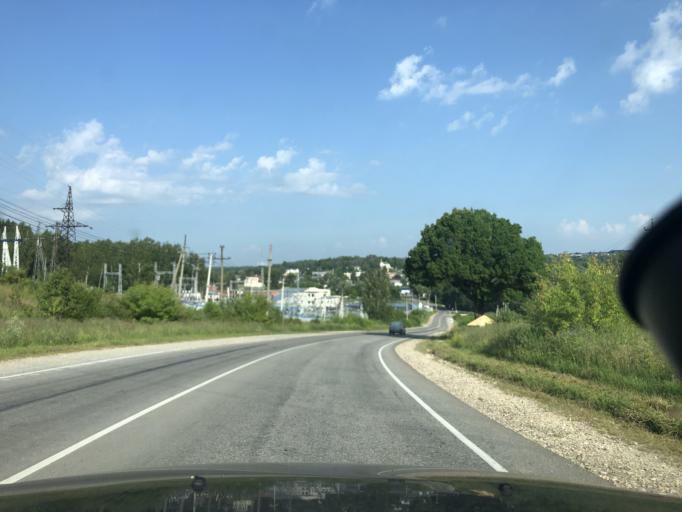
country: RU
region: Tula
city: Dubna
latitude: 54.1474
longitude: 36.9736
